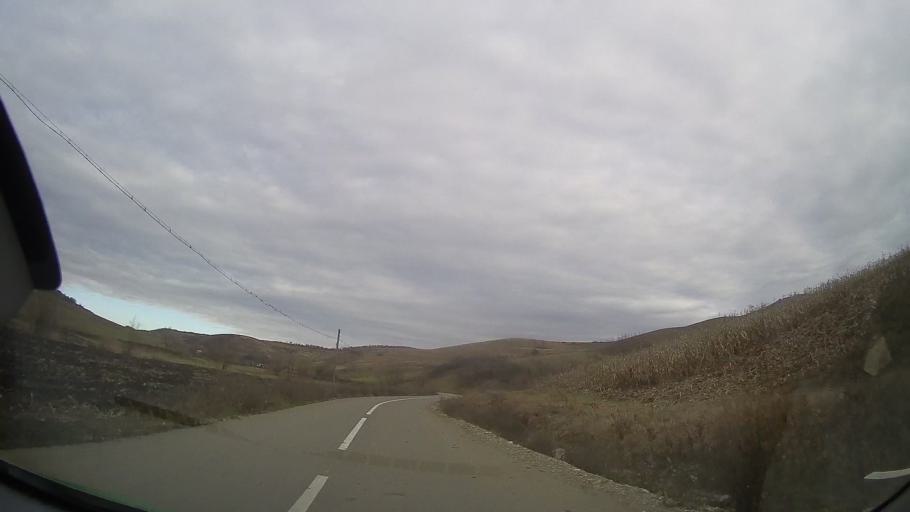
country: RO
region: Bistrita-Nasaud
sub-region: Comuna Silvasu de Campie
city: Silvasu de Campie
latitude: 46.8226
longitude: 24.3019
